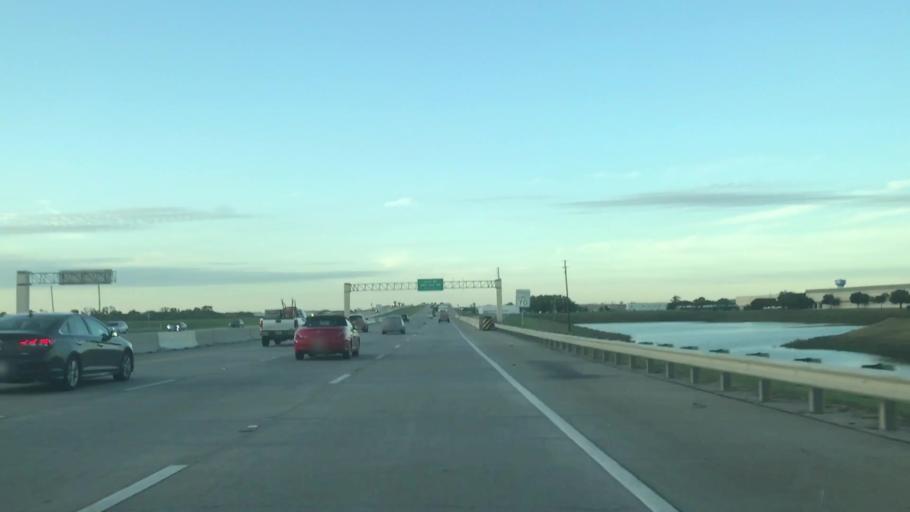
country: US
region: Texas
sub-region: Dallas County
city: Farmers Branch
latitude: 32.9293
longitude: -96.9305
